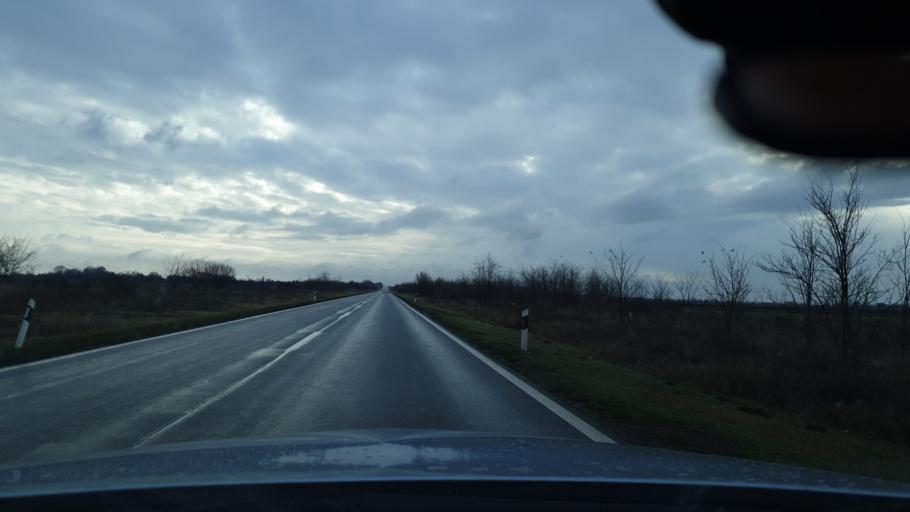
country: RS
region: Autonomna Pokrajina Vojvodina
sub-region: Juznobanatski Okrug
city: Kovin
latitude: 44.7718
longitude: 20.9428
